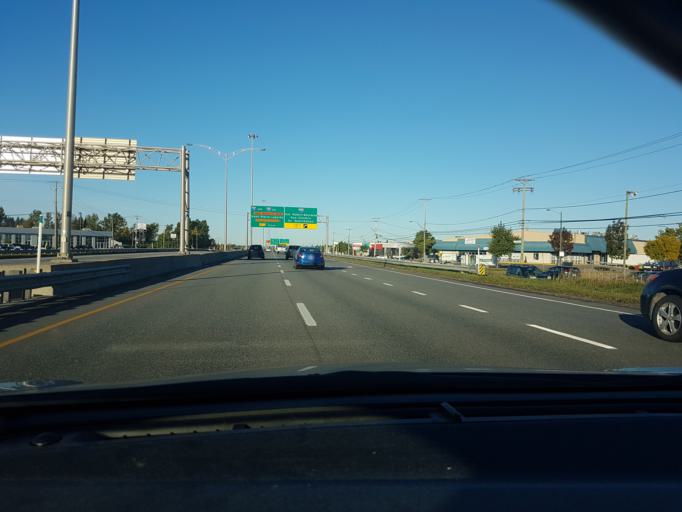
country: CA
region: Quebec
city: Quebec
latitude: 46.7955
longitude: -71.2747
